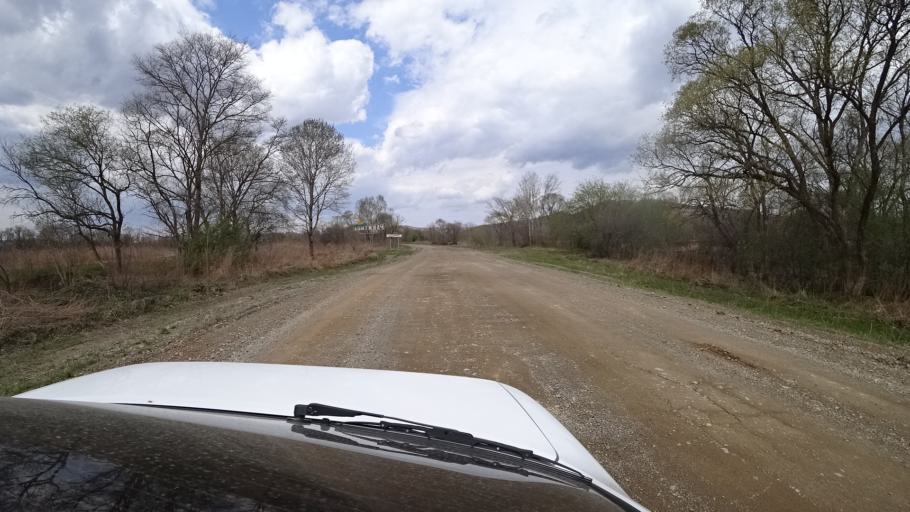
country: RU
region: Primorskiy
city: Novopokrovka
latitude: 45.6121
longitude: 134.2744
